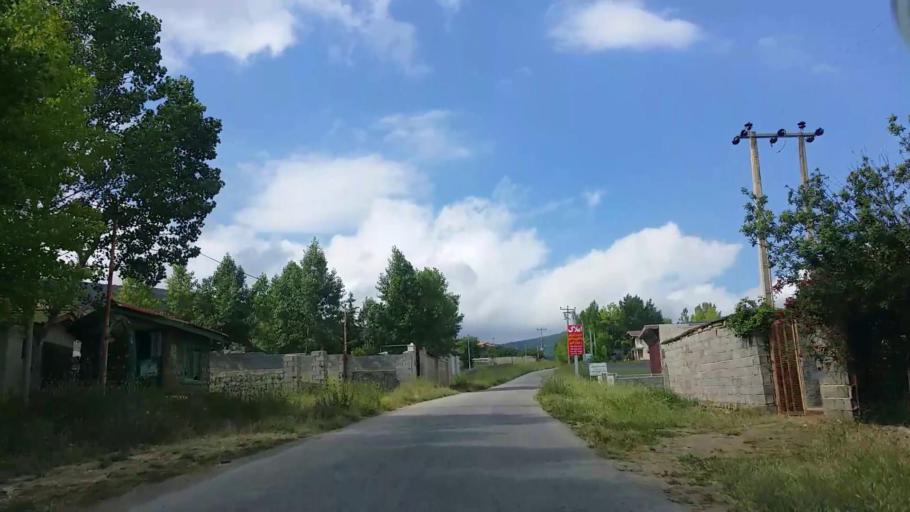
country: IR
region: Mazandaran
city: Chalus
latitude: 36.5313
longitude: 51.2690
